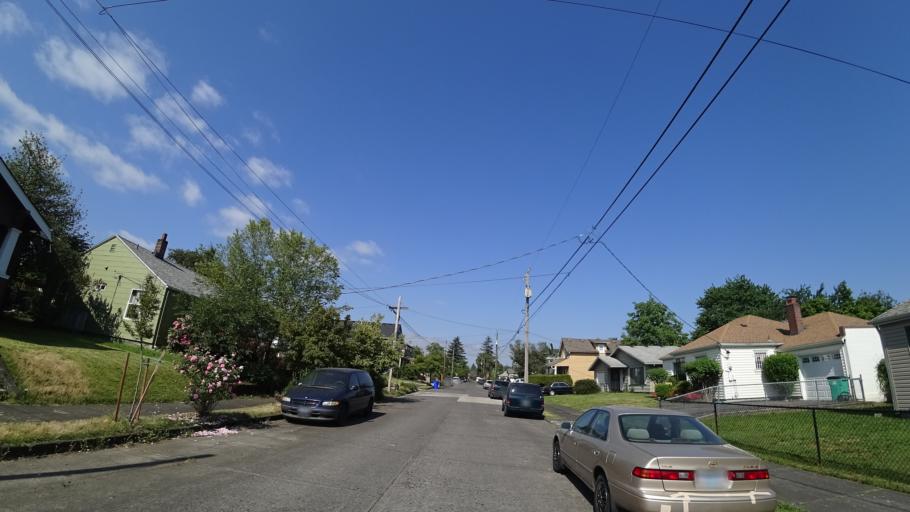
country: US
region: Oregon
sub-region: Multnomah County
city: Portland
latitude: 45.5691
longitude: -122.6485
